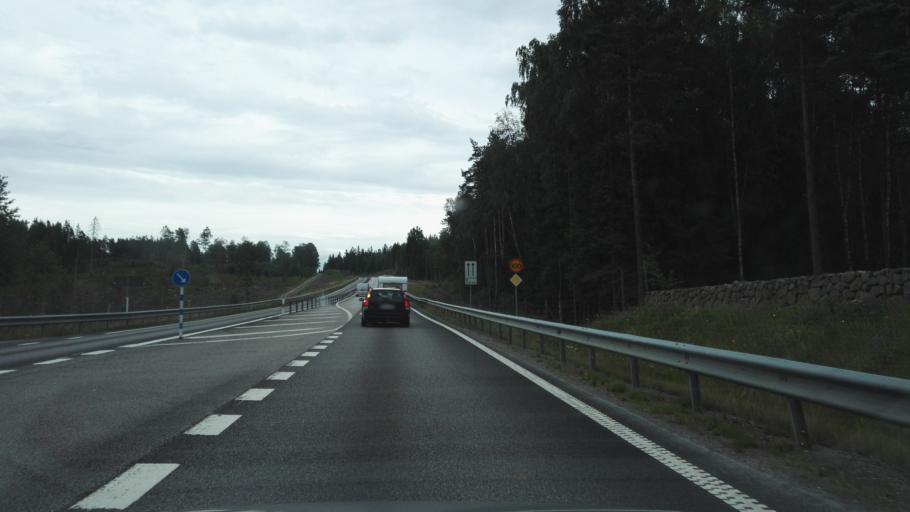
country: SE
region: Kronoberg
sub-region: Vaxjo Kommun
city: Rottne
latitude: 56.9424
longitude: 14.8987
